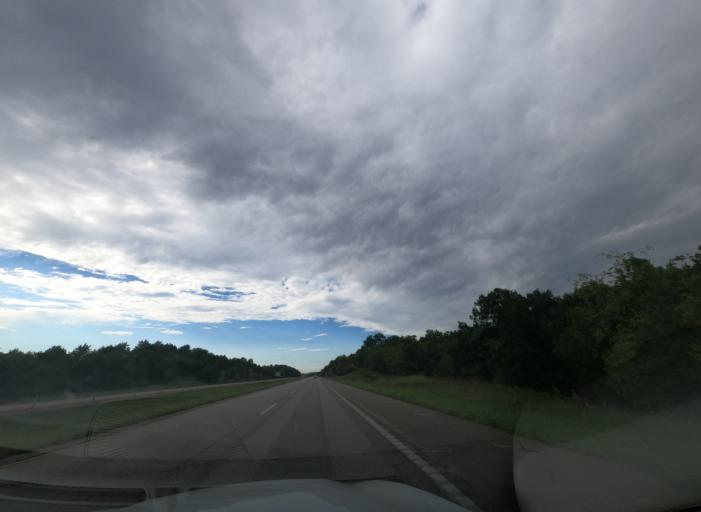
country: US
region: Missouri
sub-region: Sainte Genevieve County
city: Sainte Genevieve
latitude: 37.9812
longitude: -90.1952
